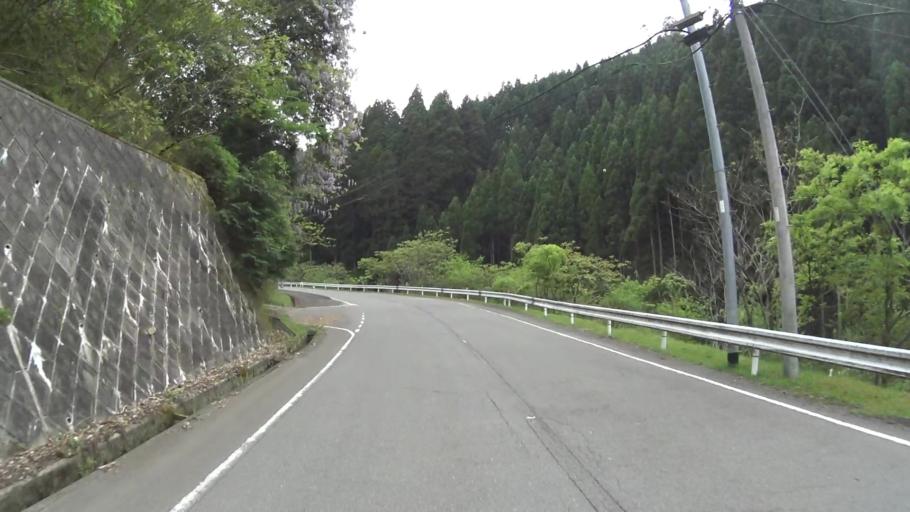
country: JP
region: Kyoto
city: Kameoka
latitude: 35.1319
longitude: 135.6195
